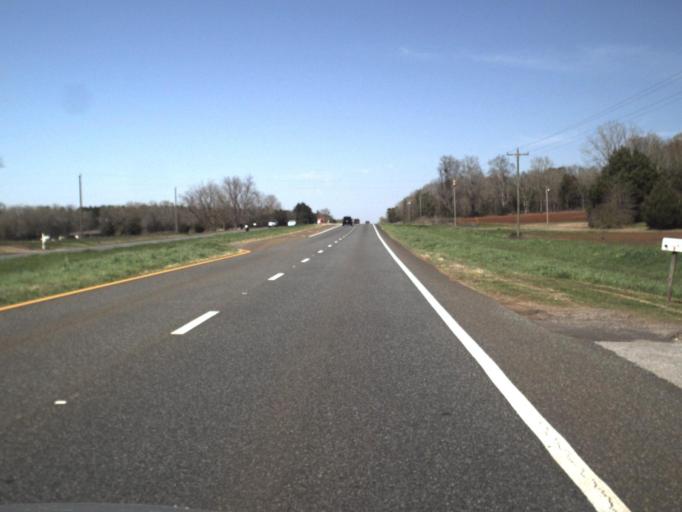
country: US
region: Florida
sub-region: Jackson County
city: Marianna
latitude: 30.8675
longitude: -85.3584
